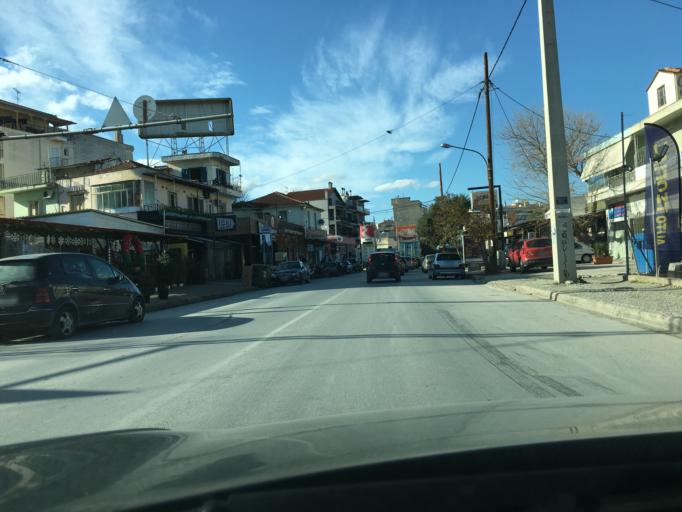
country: GR
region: Thessaly
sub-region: Nomos Larisis
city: Larisa
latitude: 39.6341
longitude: 22.4315
